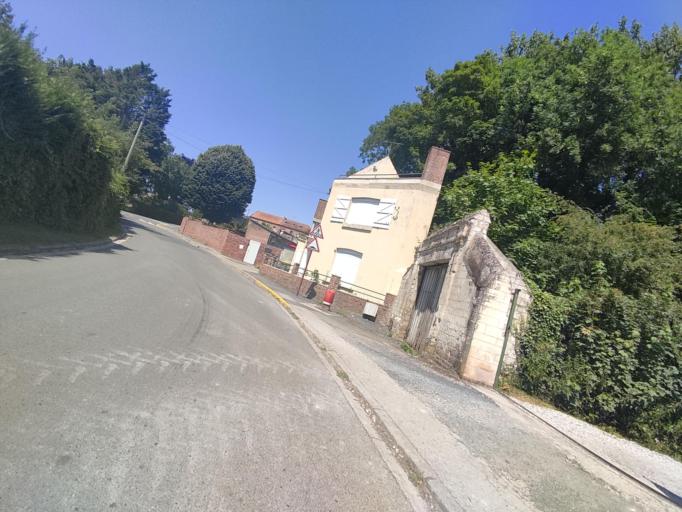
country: FR
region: Nord-Pas-de-Calais
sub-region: Departement du Pas-de-Calais
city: Maroeuil
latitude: 50.3132
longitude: 2.7030
